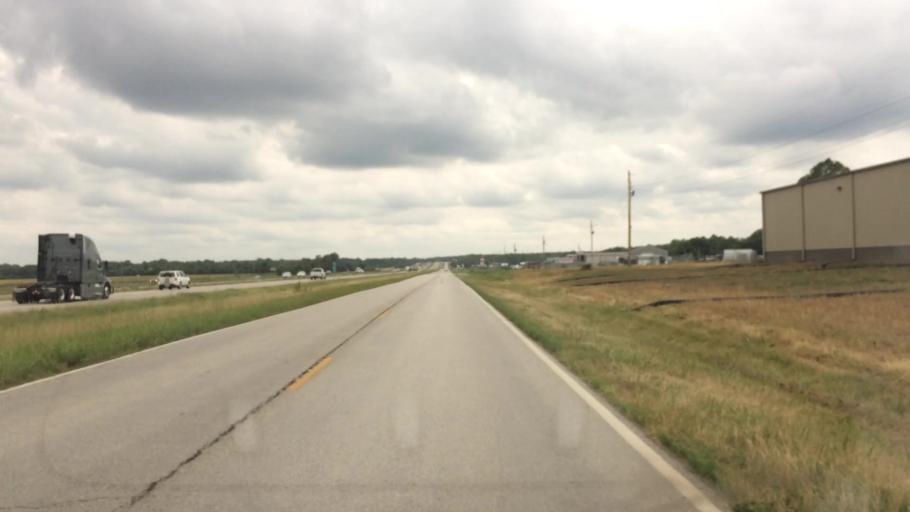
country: US
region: Missouri
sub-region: Greene County
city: Strafford
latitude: 37.2964
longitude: -93.0194
